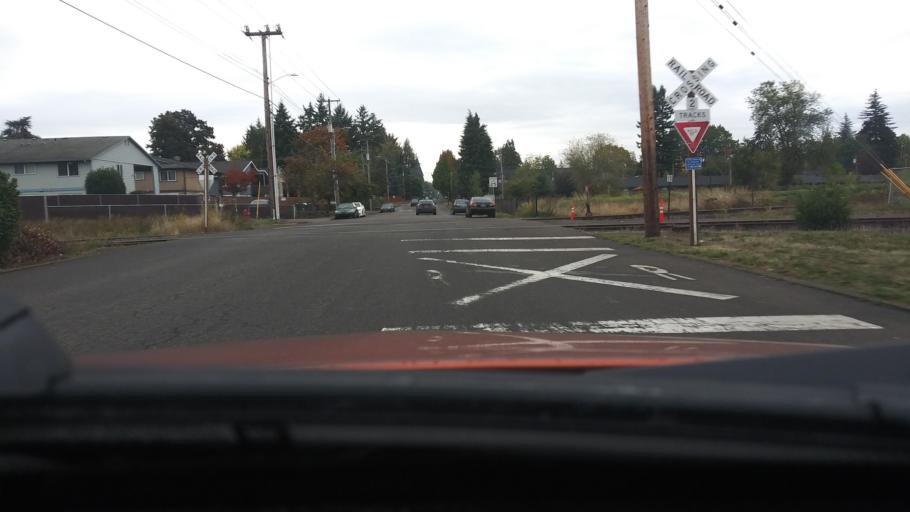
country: US
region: Oregon
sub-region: Washington County
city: Forest Grove
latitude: 45.5238
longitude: -123.0992
